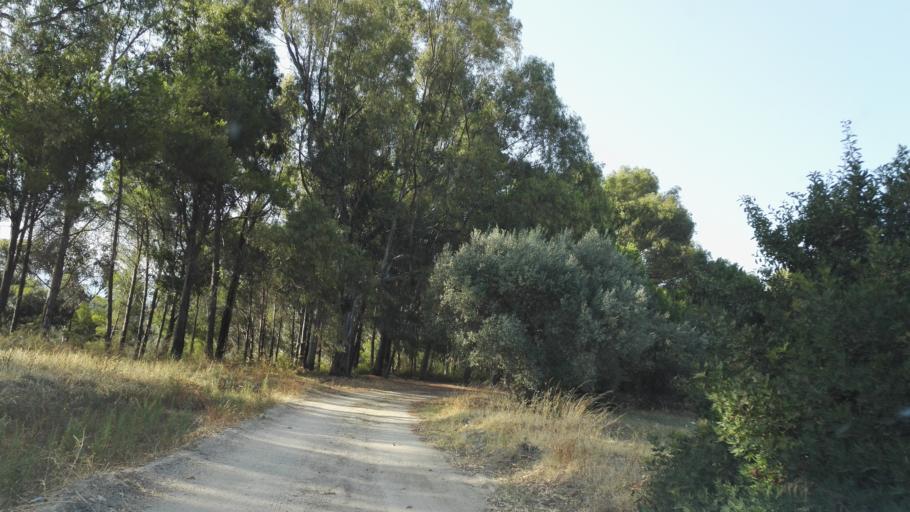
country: IT
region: Calabria
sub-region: Provincia di Reggio Calabria
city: Riace Marina
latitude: 38.3747
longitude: 16.4955
